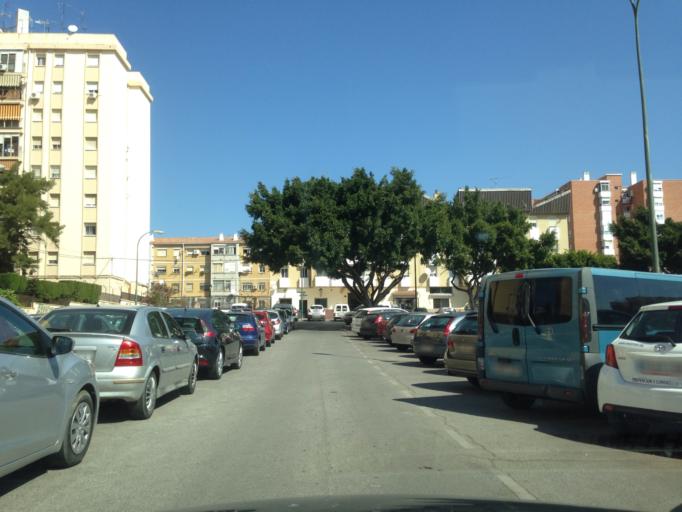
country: ES
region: Andalusia
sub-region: Provincia de Malaga
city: Malaga
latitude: 36.7157
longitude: -4.4515
